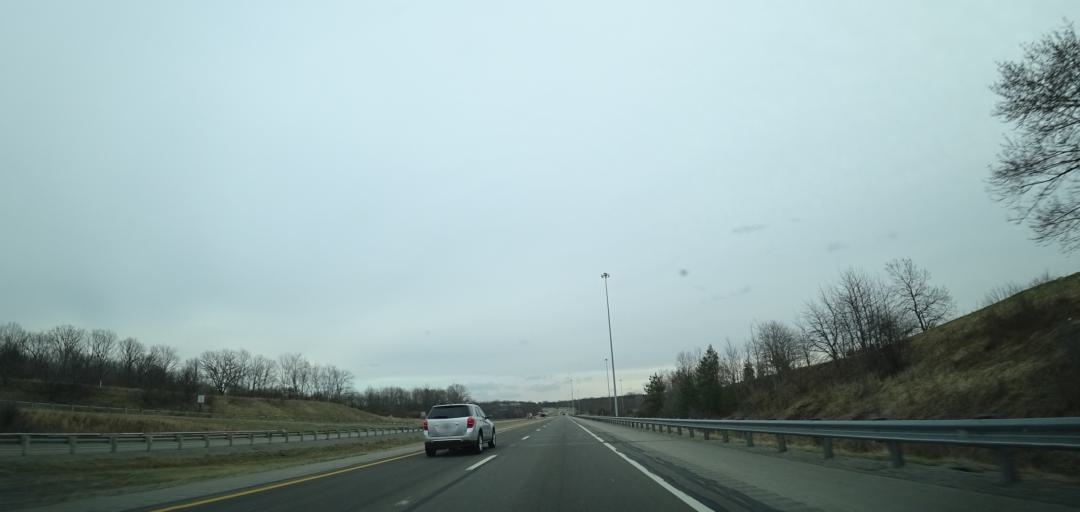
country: US
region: Ohio
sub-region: Mahoning County
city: Boardman
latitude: 40.9554
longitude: -80.6398
